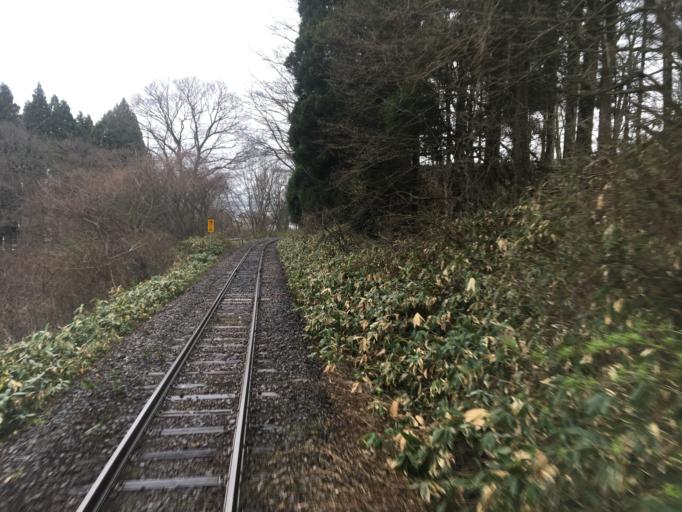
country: JP
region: Akita
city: Takanosu
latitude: 40.2033
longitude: 140.3459
